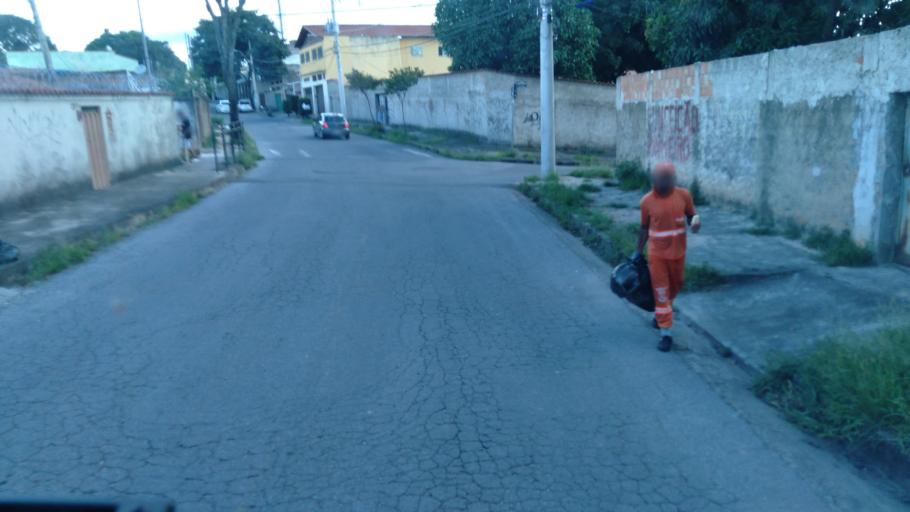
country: BR
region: Minas Gerais
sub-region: Belo Horizonte
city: Belo Horizonte
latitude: -19.8542
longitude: -43.9112
